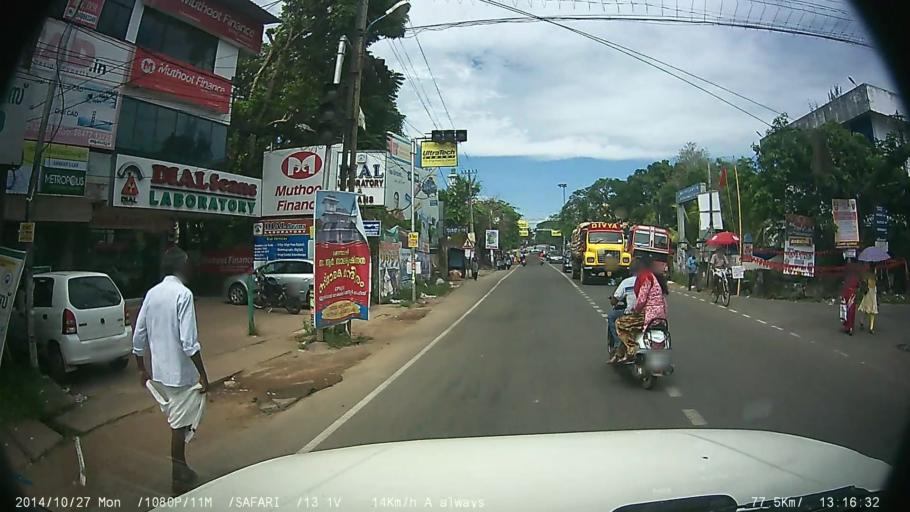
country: IN
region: Kerala
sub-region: Alappuzha
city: Alleppey
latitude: 9.4905
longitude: 76.3385
